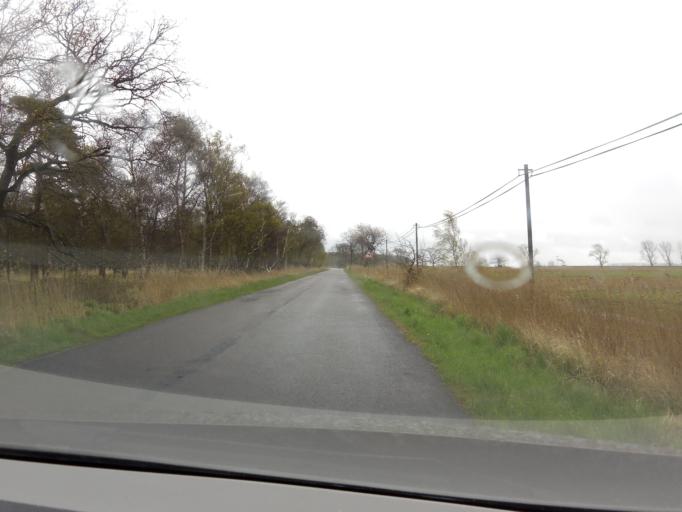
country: DE
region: Mecklenburg-Vorpommern
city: Barth
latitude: 54.4193
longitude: 12.7489
